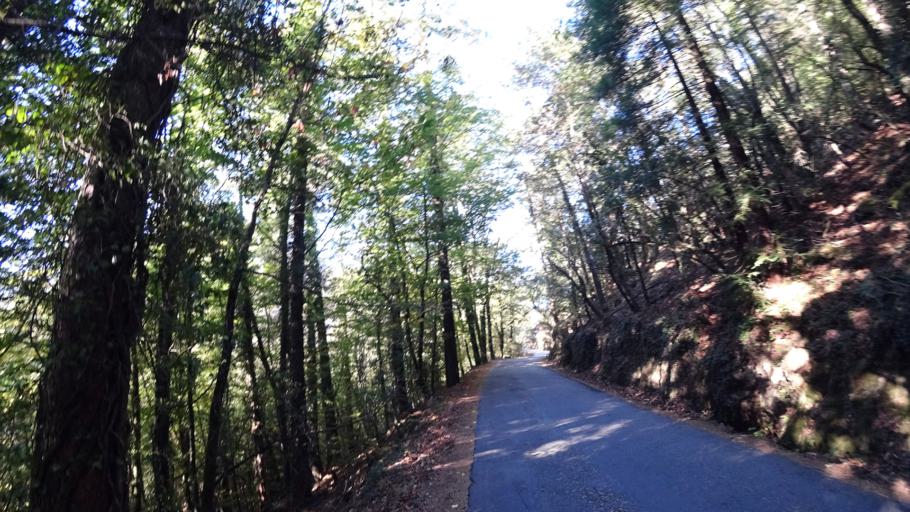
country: ES
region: Galicia
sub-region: Provincia de Ourense
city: Lobios
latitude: 41.7947
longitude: -8.1342
